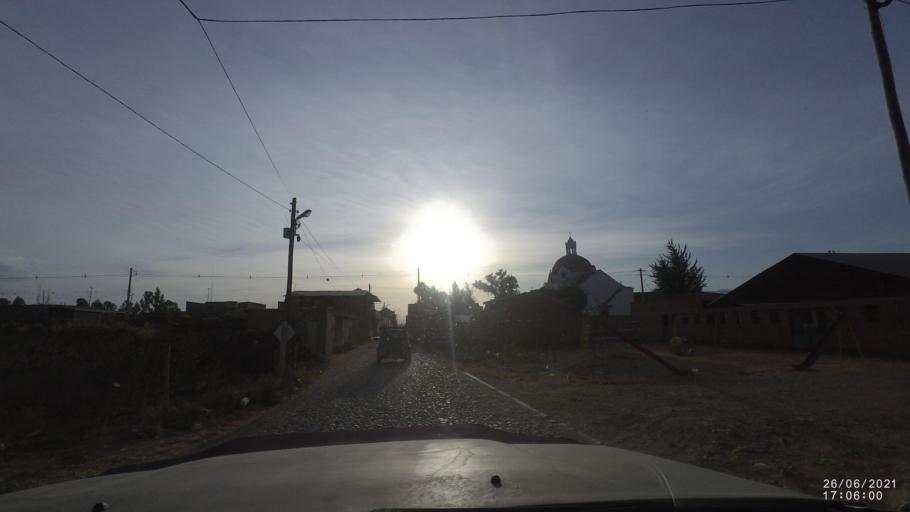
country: BO
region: Cochabamba
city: Cliza
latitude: -17.6277
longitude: -65.9257
